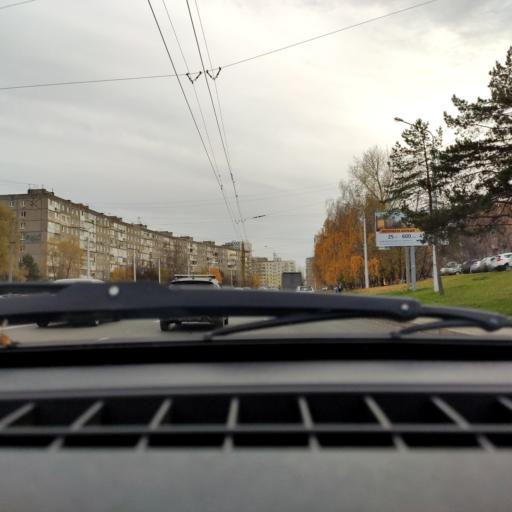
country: RU
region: Bashkortostan
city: Ufa
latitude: 54.7724
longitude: 56.0335
